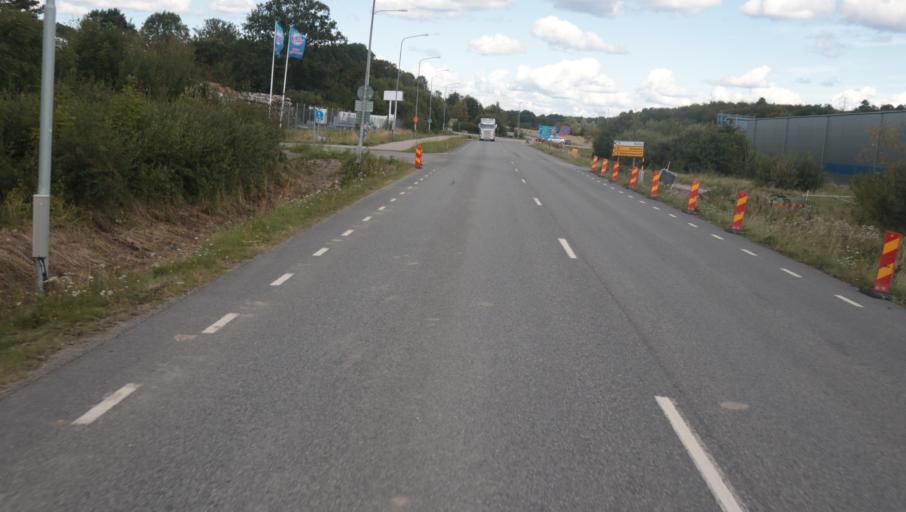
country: SE
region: Blekinge
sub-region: Karlshamns Kommun
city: Karlshamn
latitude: 56.1705
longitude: 14.8194
